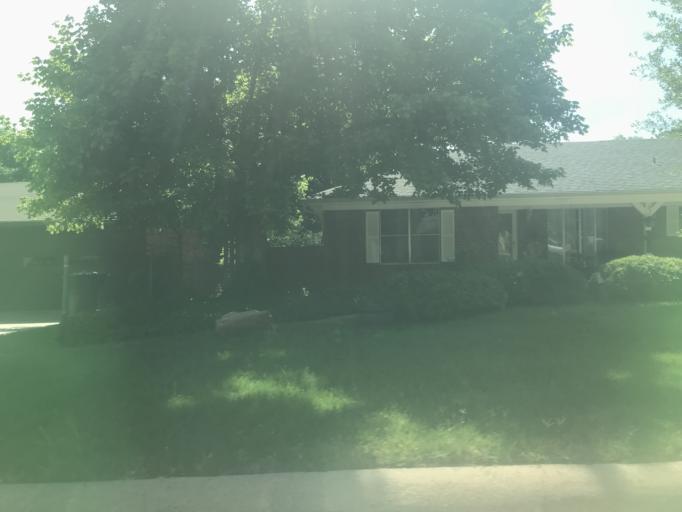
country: US
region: Texas
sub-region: Taylor County
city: Abilene
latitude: 32.4362
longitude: -99.7492
